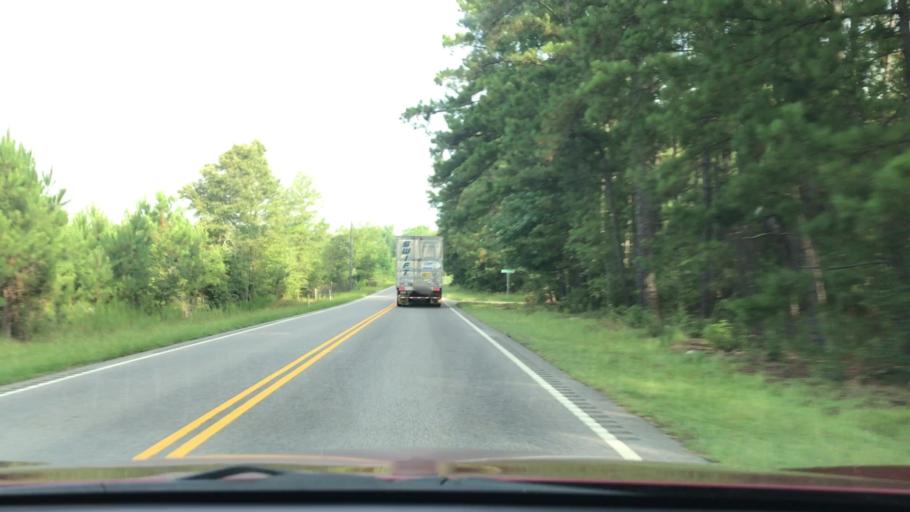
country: US
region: South Carolina
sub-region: Barnwell County
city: Williston
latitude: 33.6214
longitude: -81.2921
